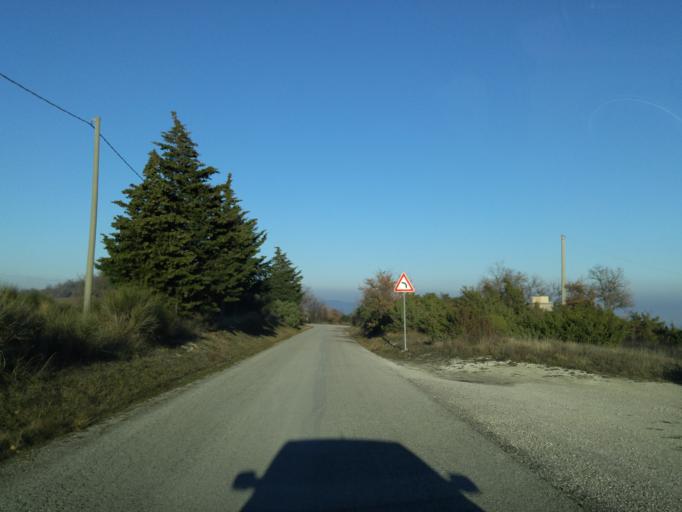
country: IT
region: The Marches
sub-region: Provincia di Pesaro e Urbino
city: Isola del Piano
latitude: 43.7163
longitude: 12.7486
